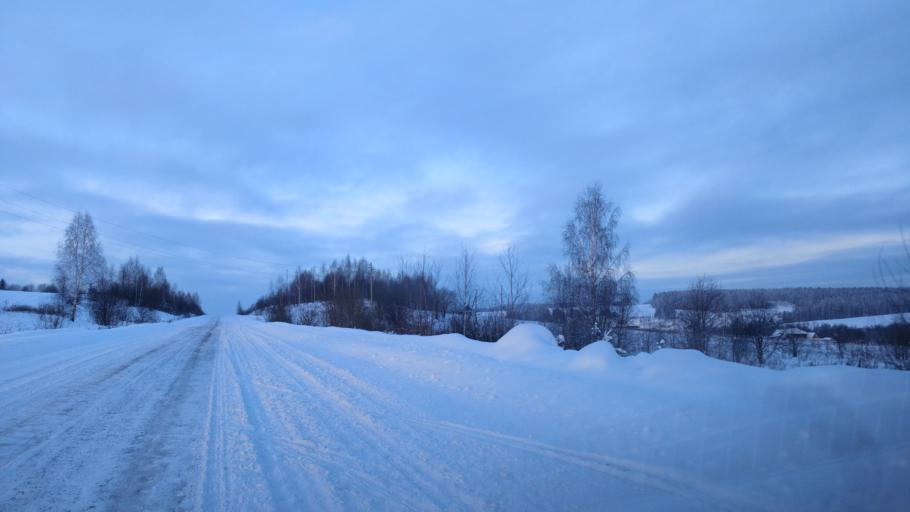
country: RU
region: Perm
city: Verkhnechusovskiye Gorodki
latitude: 58.2074
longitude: 57.1433
